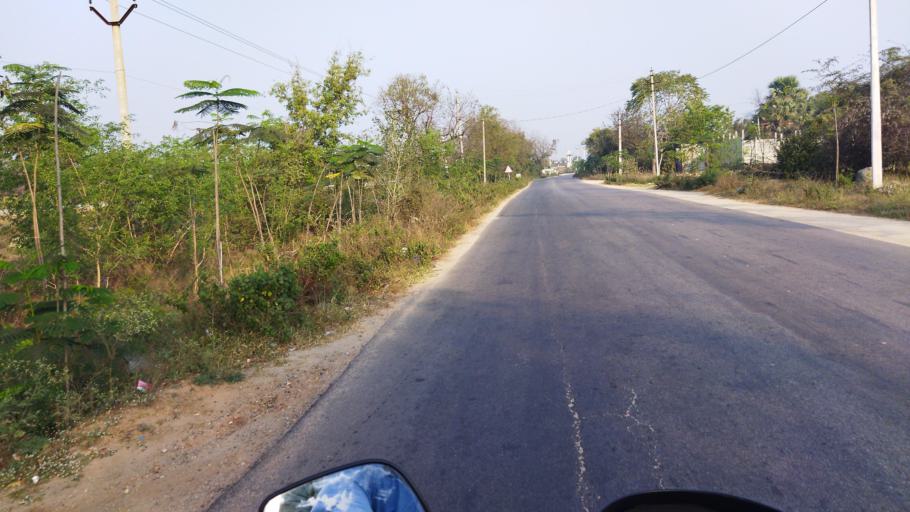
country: IN
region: Telangana
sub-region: Nalgonda
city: Nalgonda
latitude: 17.2418
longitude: 79.1146
